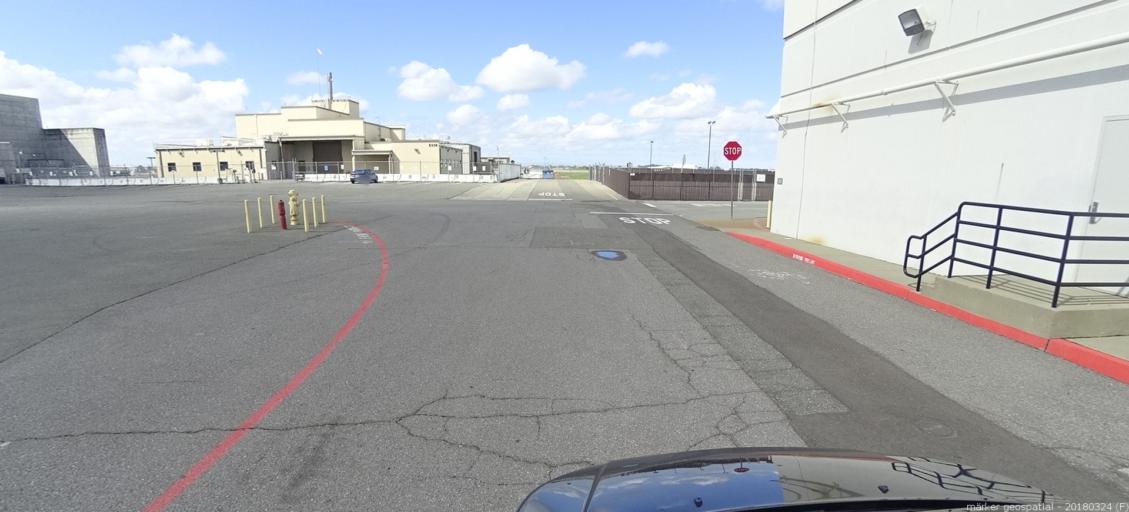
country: US
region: California
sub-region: Sacramento County
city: North Highlands
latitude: 38.6652
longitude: -121.3923
